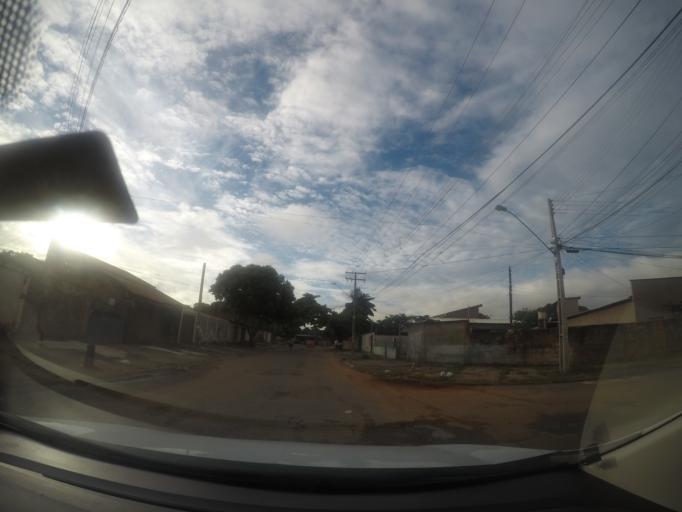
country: BR
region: Goias
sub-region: Goiania
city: Goiania
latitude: -16.6859
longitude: -49.3101
